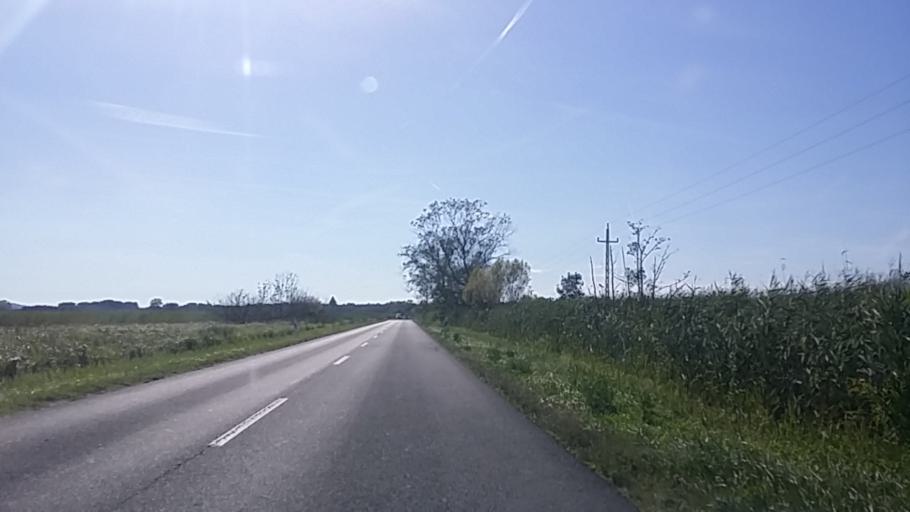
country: HU
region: Zala
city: Sarmellek
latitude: 46.7074
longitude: 17.1897
